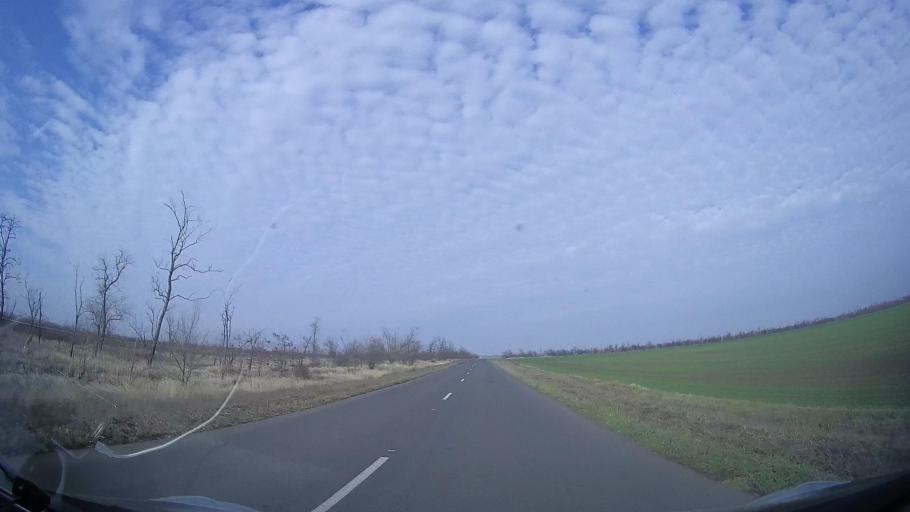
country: RU
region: Rostov
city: Gigant
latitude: 46.8563
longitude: 41.2820
